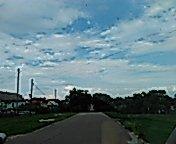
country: RU
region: Penza
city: Lermontovo
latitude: 52.9930
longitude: 43.6624
